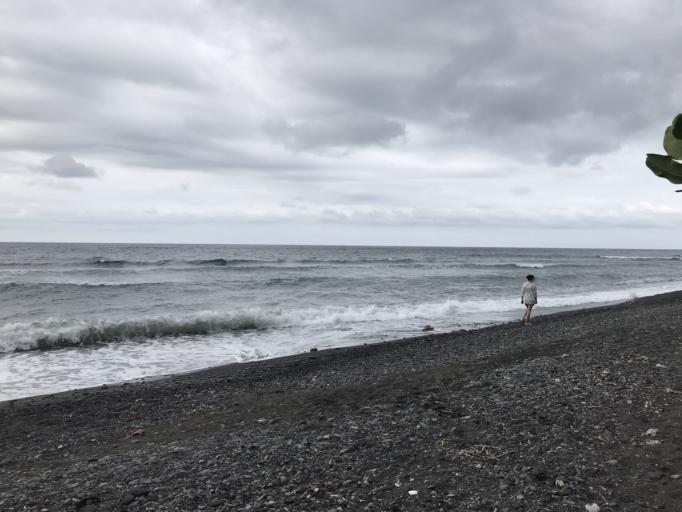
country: ID
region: Bali
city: Biaslantang Kaler
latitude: -8.3349
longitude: 115.6560
